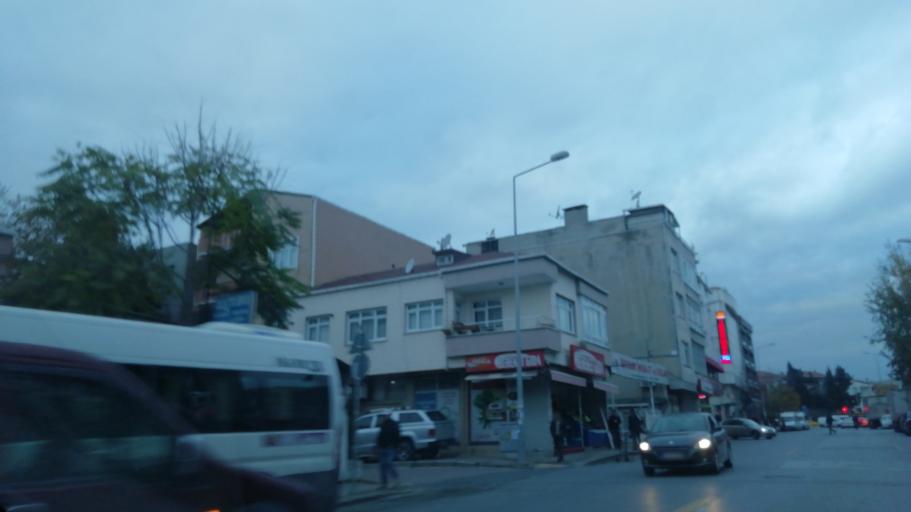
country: TR
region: Istanbul
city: Bahcelievler
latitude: 41.0125
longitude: 28.8265
